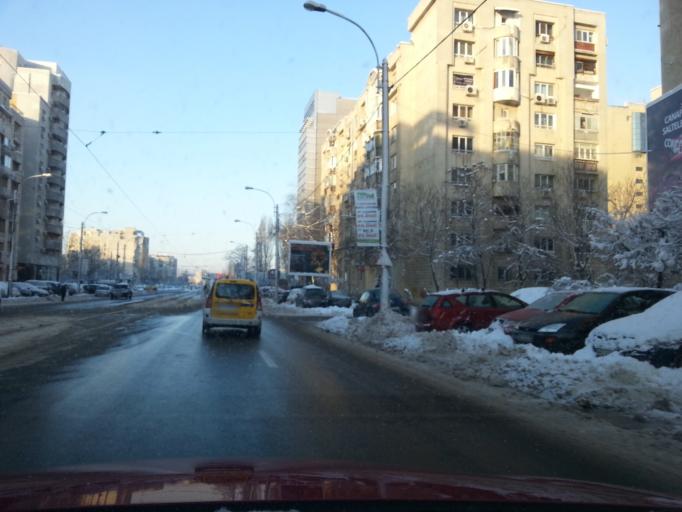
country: RO
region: Bucuresti
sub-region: Municipiul Bucuresti
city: Bucharest
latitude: 44.4240
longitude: 26.1210
